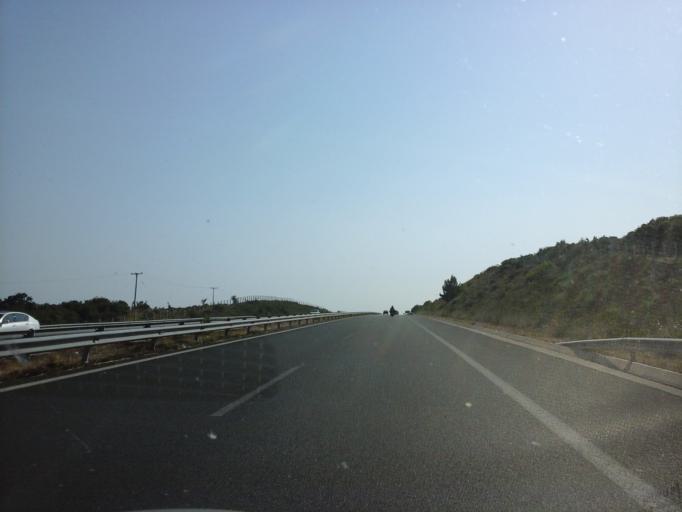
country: GR
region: East Macedonia and Thrace
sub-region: Nomos Evrou
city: Alexandroupoli
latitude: 40.8724
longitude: 25.8423
